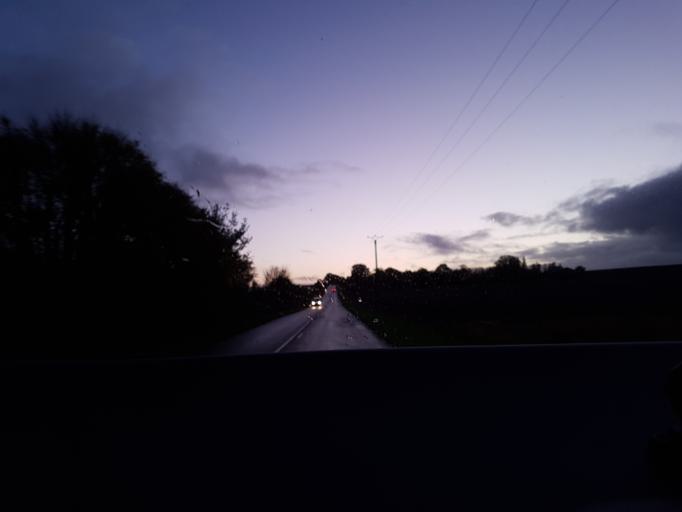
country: FR
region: Poitou-Charentes
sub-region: Departement des Deux-Sevres
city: Lezay
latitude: 46.2587
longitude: -0.0184
